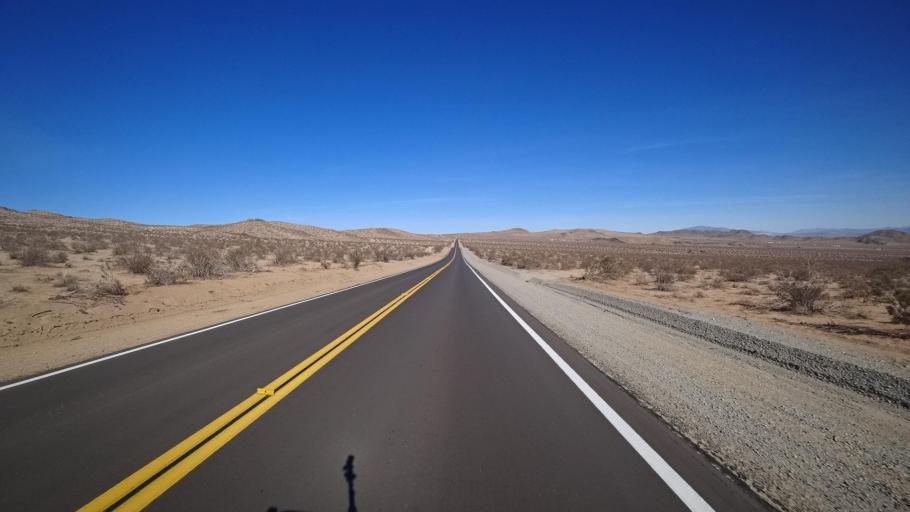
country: US
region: California
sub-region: Kern County
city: Ridgecrest
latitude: 35.5322
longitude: -117.5918
